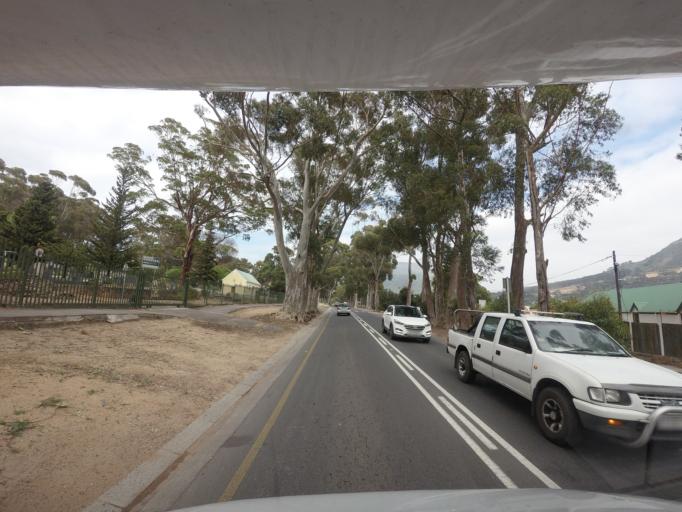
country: ZA
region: Western Cape
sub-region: City of Cape Town
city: Constantia
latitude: -34.0228
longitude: 18.3643
